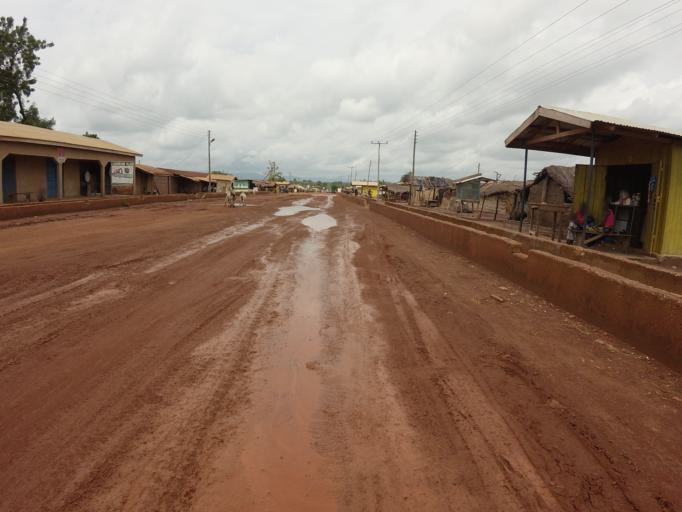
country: GH
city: Kpandae
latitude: 8.4005
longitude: 0.4053
